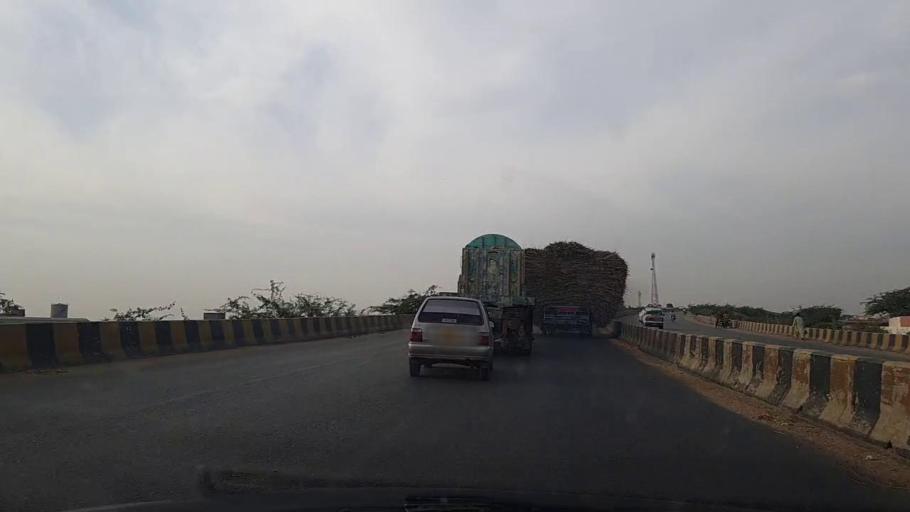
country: PK
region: Sindh
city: Gharo
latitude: 24.8421
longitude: 67.4311
